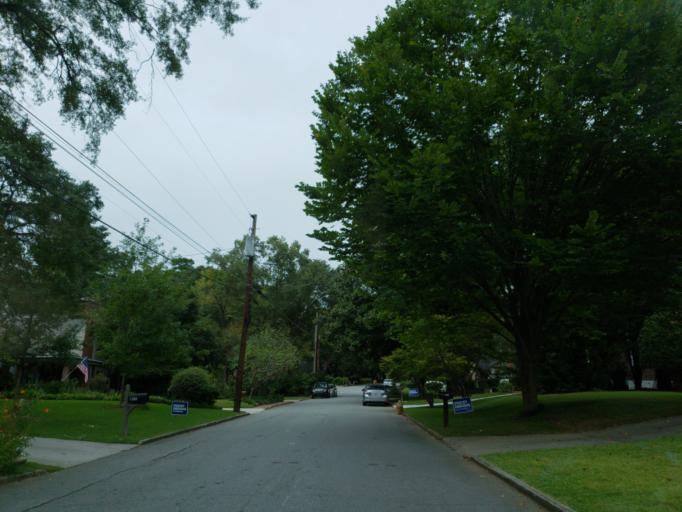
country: US
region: Georgia
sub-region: DeKalb County
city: Druid Hills
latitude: 33.7917
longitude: -84.3612
